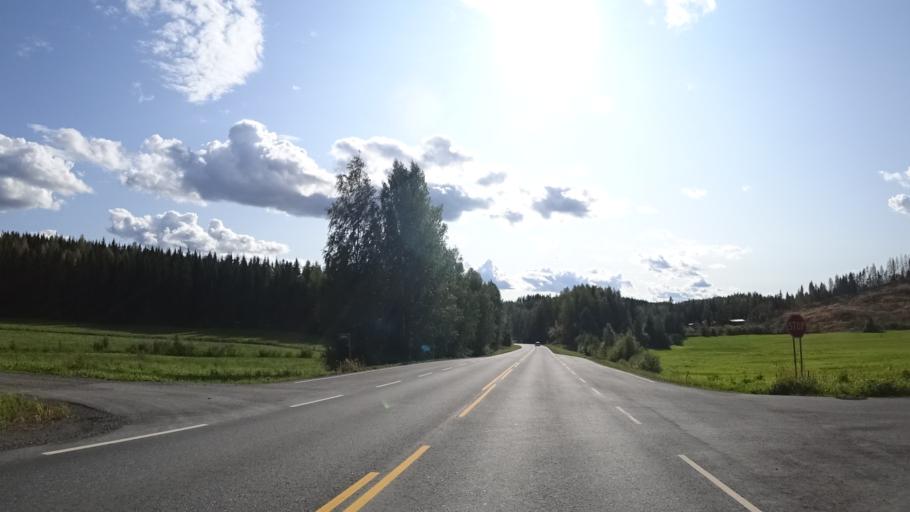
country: FI
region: North Karelia
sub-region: Keski-Karjala
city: Tohmajaervi
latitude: 62.2107
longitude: 30.2896
